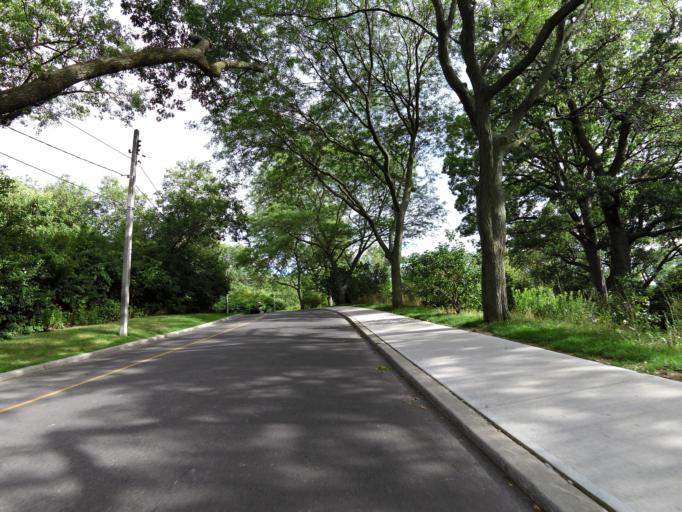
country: CA
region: Ontario
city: Toronto
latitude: 43.6425
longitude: -79.4634
